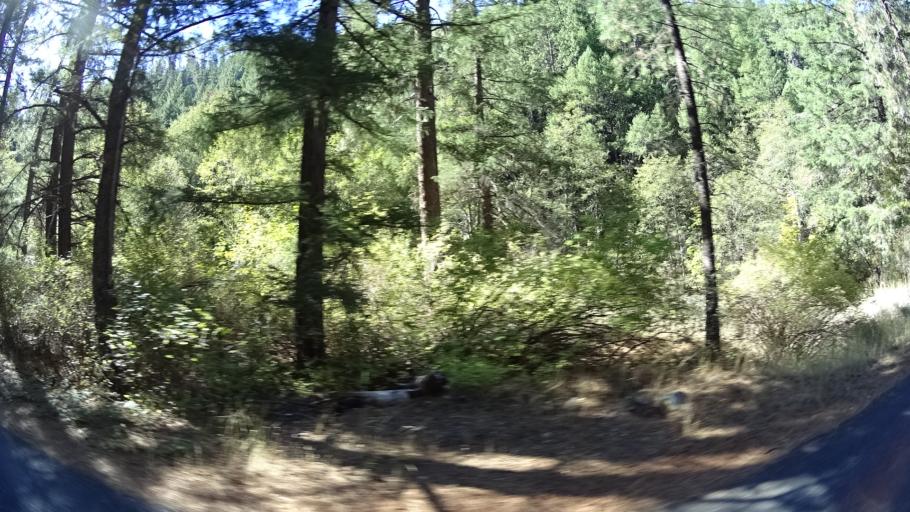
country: US
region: California
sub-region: Trinity County
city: Weaverville
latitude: 41.1478
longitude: -123.1091
